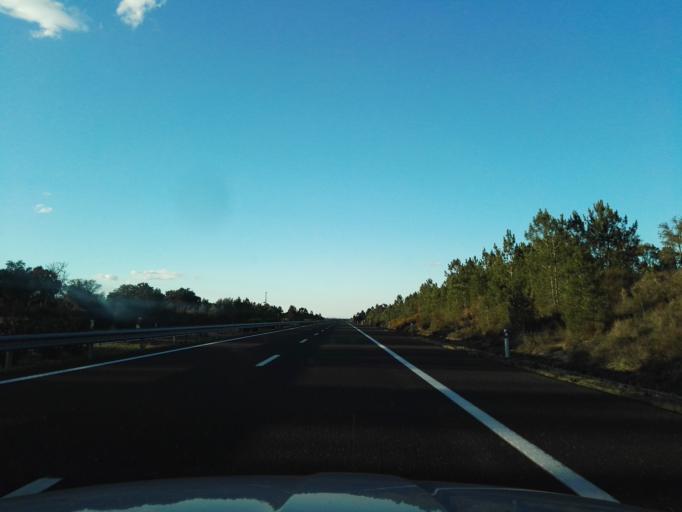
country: PT
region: Santarem
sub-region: Benavente
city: Poceirao
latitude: 38.8017
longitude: -8.6984
